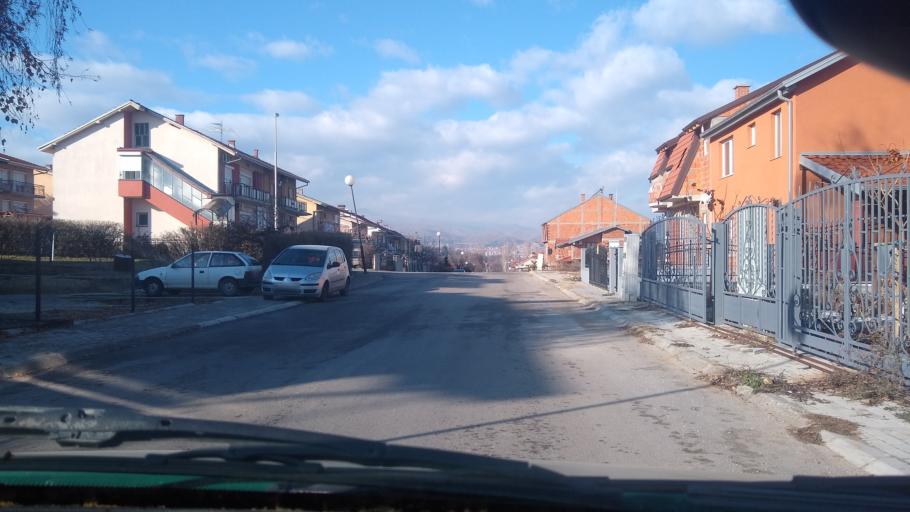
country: MK
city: Bistrica
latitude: 41.0053
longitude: 21.3492
